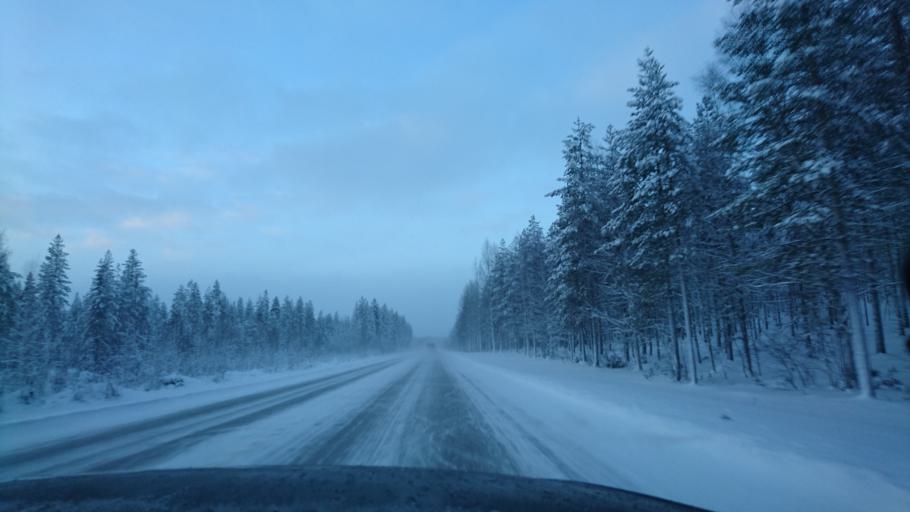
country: FI
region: Northern Ostrobothnia
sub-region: Koillismaa
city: Taivalkoski
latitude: 65.4874
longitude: 27.8606
